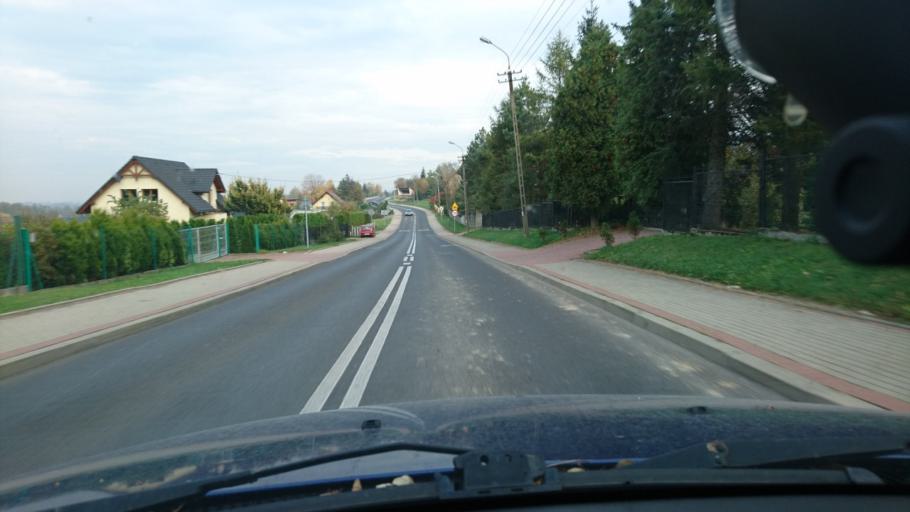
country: PL
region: Silesian Voivodeship
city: Janowice
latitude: 49.8411
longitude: 19.1008
